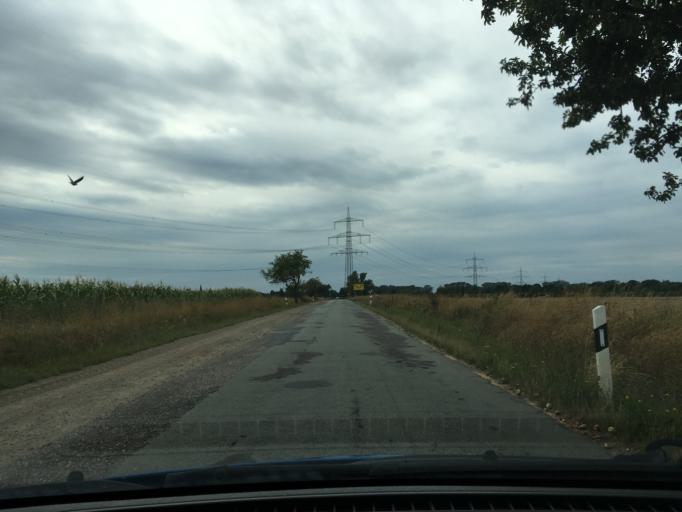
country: DE
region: Mecklenburg-Vorpommern
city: Wittenburg
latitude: 53.5164
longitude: 11.1004
